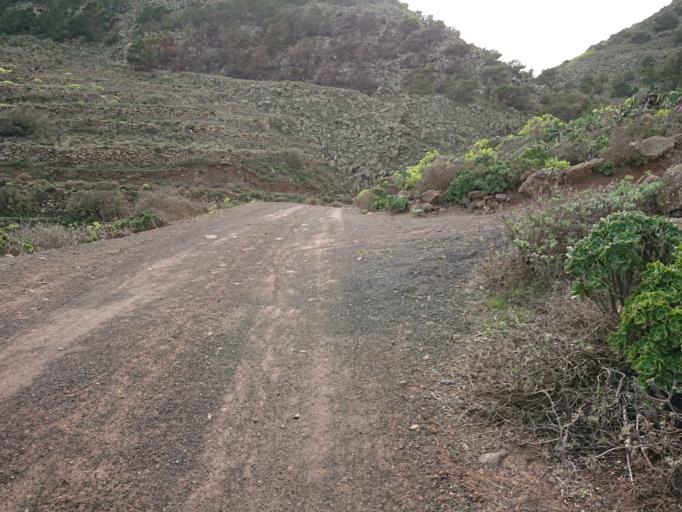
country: ES
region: Canary Islands
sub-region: Provincia de Las Palmas
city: Haria
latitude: 29.1334
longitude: -13.5181
